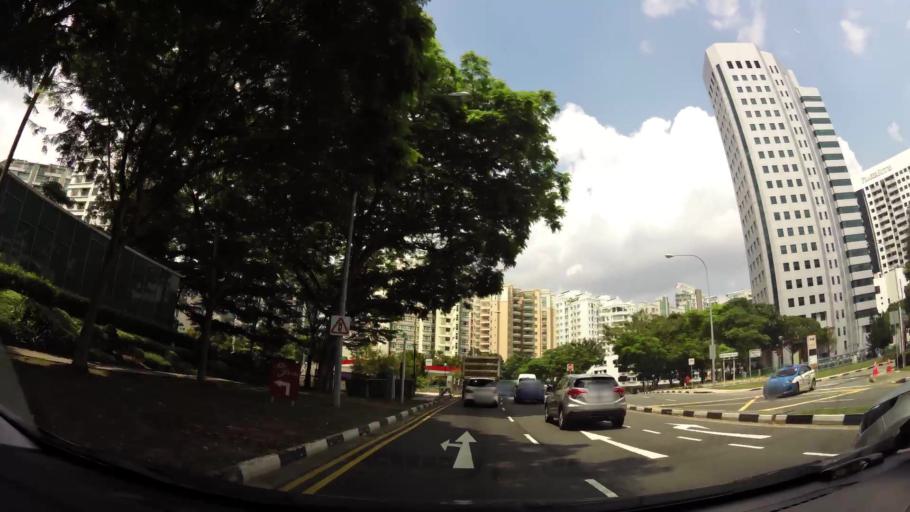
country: SG
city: Singapore
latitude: 1.2920
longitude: 103.8259
